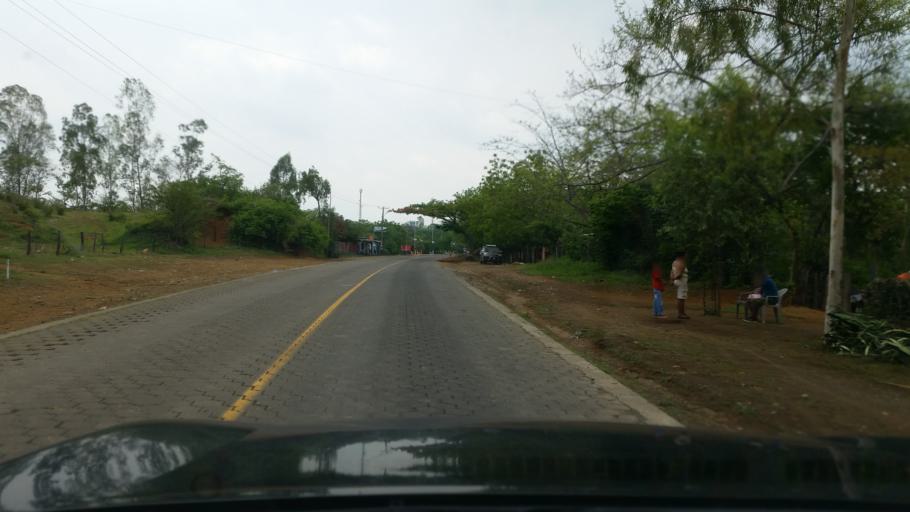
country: NI
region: Managua
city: Carlos Fonseca Amador
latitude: 11.8941
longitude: -86.5137
